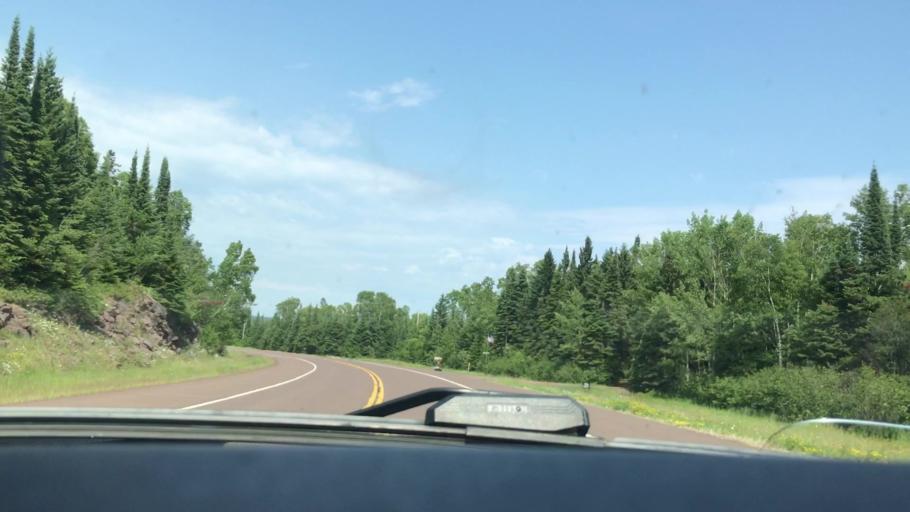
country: US
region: Minnesota
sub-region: Cook County
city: Grand Marais
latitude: 47.7780
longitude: -90.1919
